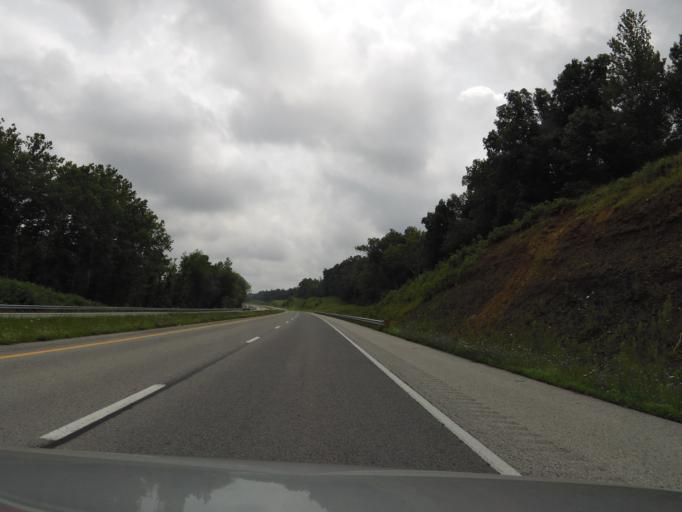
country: US
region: Kentucky
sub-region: Ohio County
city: Oak Grove
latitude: 37.3924
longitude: -86.7500
